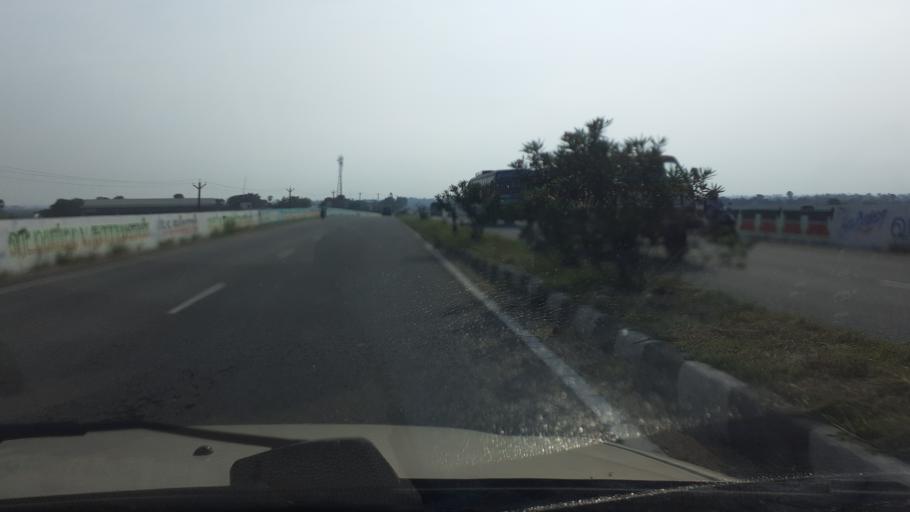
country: IN
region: Tamil Nadu
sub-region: Tirunelveli Kattabo
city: Tirunelveli
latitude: 8.6411
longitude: 77.7053
